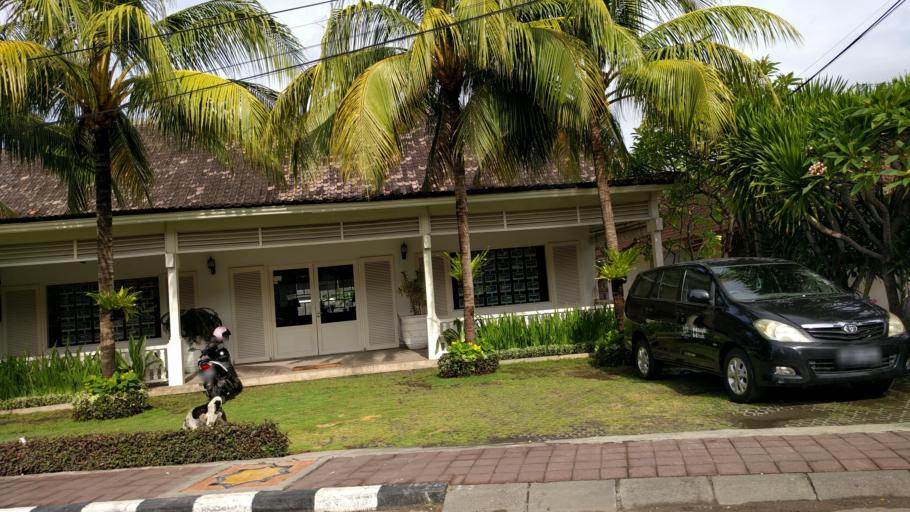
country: ID
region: Bali
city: Kuta
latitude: -8.6842
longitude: 115.1571
